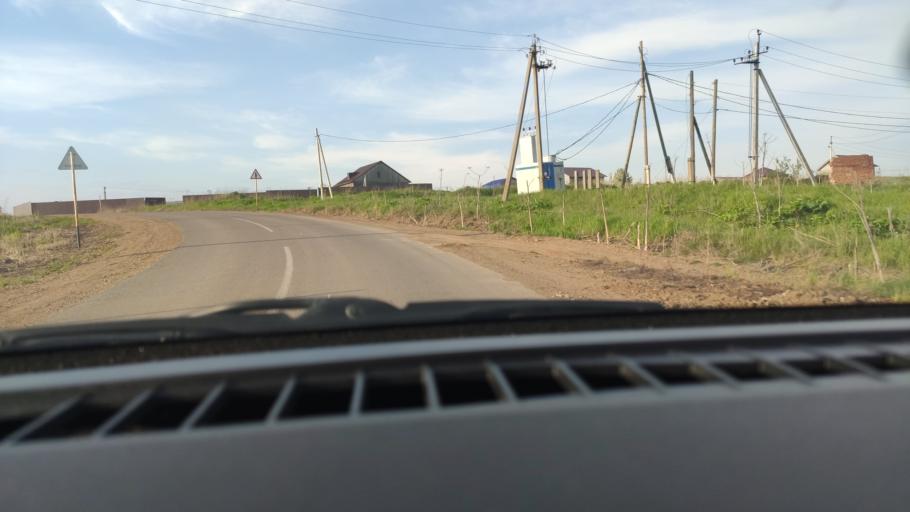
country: RU
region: Perm
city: Kultayevo
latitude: 57.8975
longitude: 55.9938
